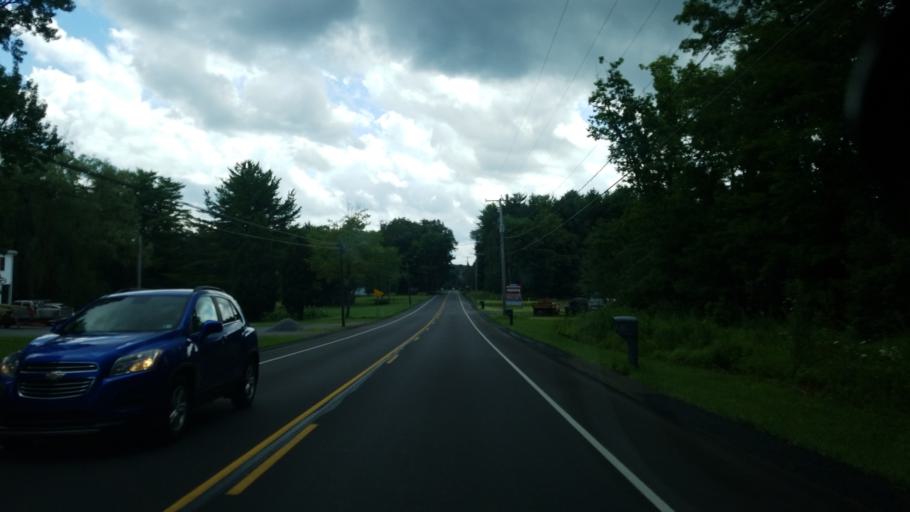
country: US
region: Pennsylvania
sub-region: Jefferson County
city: Brookville
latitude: 41.2548
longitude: -79.1087
